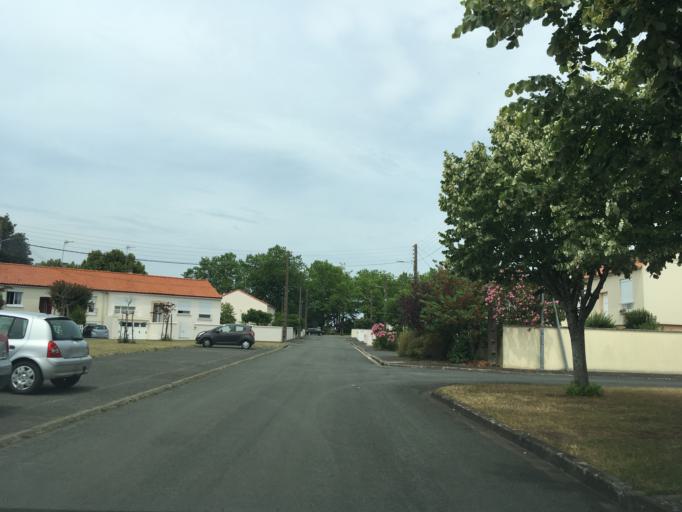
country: FR
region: Poitou-Charentes
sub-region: Departement des Deux-Sevres
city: Niort
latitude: 46.3209
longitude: -0.4879
